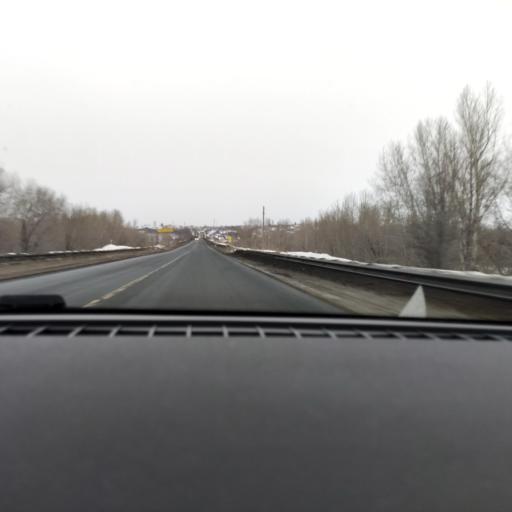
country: RU
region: Samara
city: Smyshlyayevka
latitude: 53.2285
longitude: 50.4928
